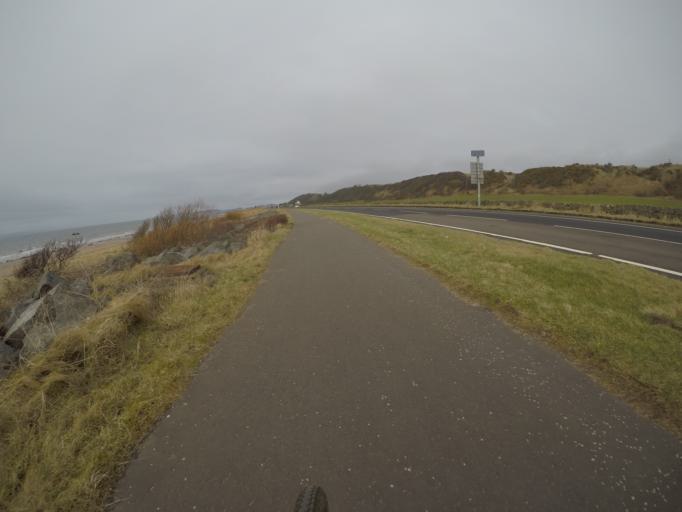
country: GB
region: Scotland
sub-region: North Ayrshire
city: West Kilbride
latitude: 55.6616
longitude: -4.8323
